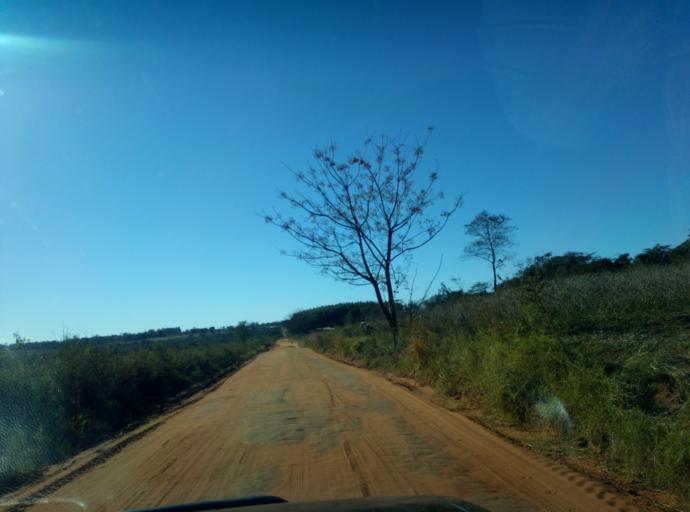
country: PY
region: Caaguazu
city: Doctor Cecilio Baez
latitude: -25.1626
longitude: -56.2658
